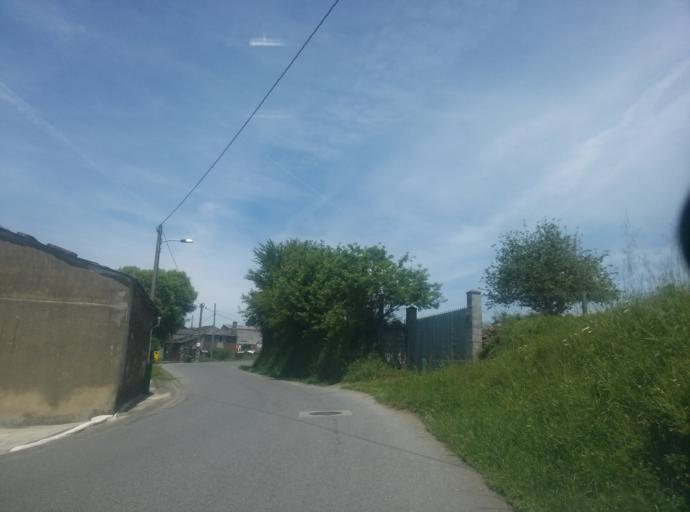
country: ES
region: Galicia
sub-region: Provincia de Lugo
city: Lugo
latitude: 43.0338
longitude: -7.5764
